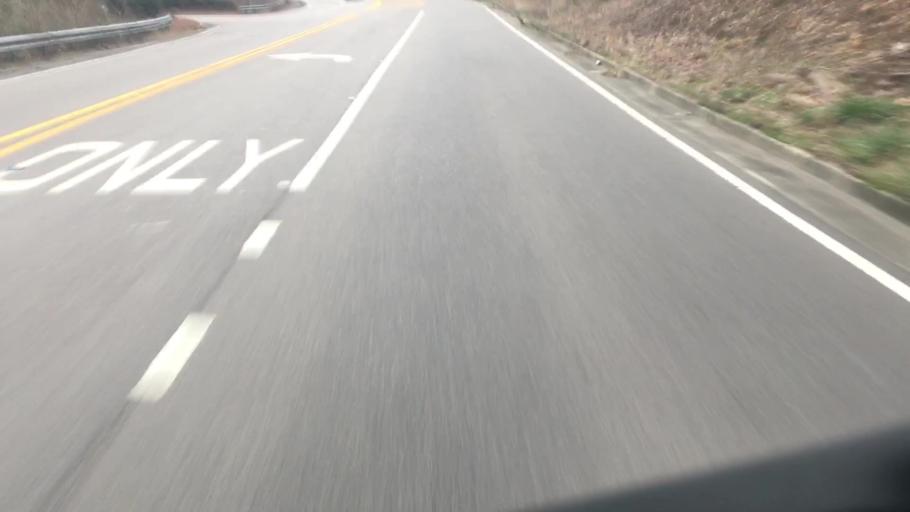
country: US
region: Alabama
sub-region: Jefferson County
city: Vestavia Hills
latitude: 33.4557
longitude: -86.7635
